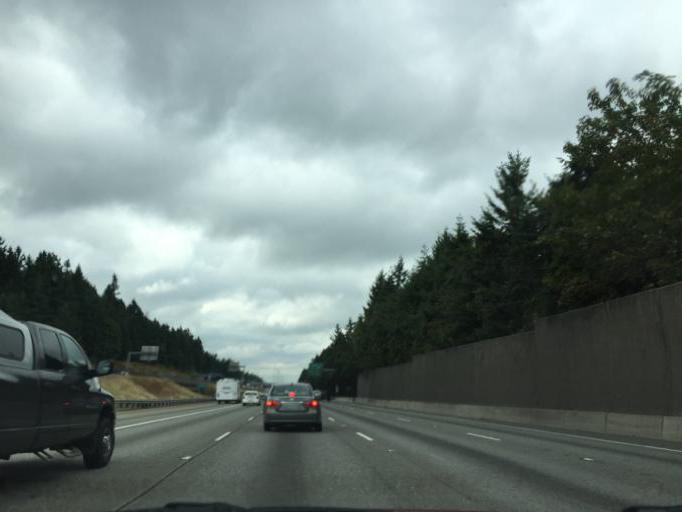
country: US
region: Washington
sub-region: King County
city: Federal Way
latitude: 47.3018
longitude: -122.3028
